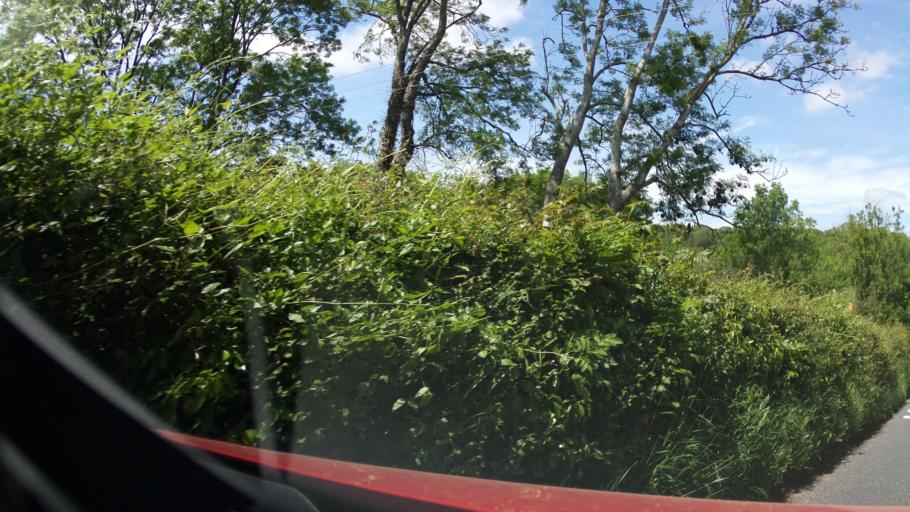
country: GB
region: Wales
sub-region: Monmouthshire
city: Monmouth
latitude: 51.7982
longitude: -2.7187
